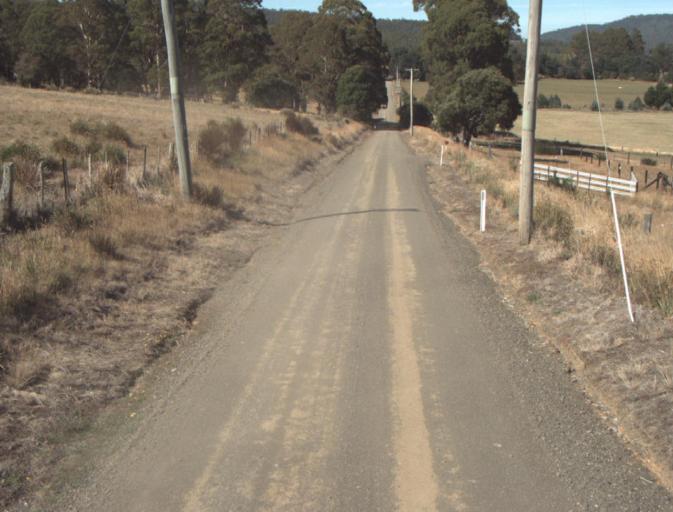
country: AU
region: Tasmania
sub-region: Launceston
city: Newstead
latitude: -41.3127
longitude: 147.3211
